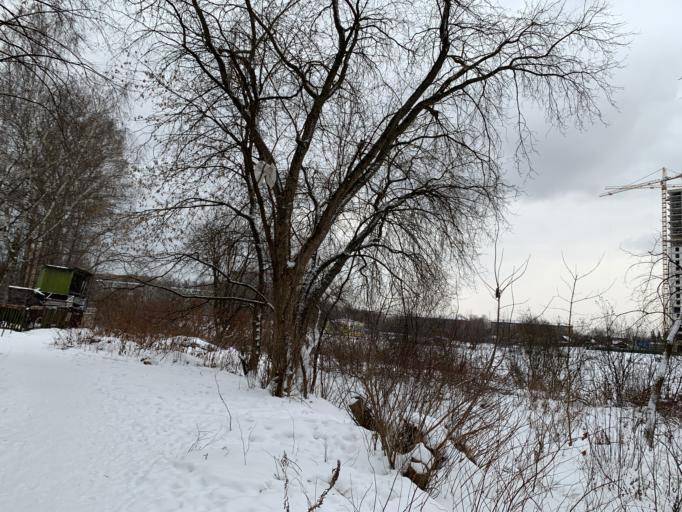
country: RU
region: Moskovskaya
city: Pushkino
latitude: 56.0021
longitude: 37.8663
